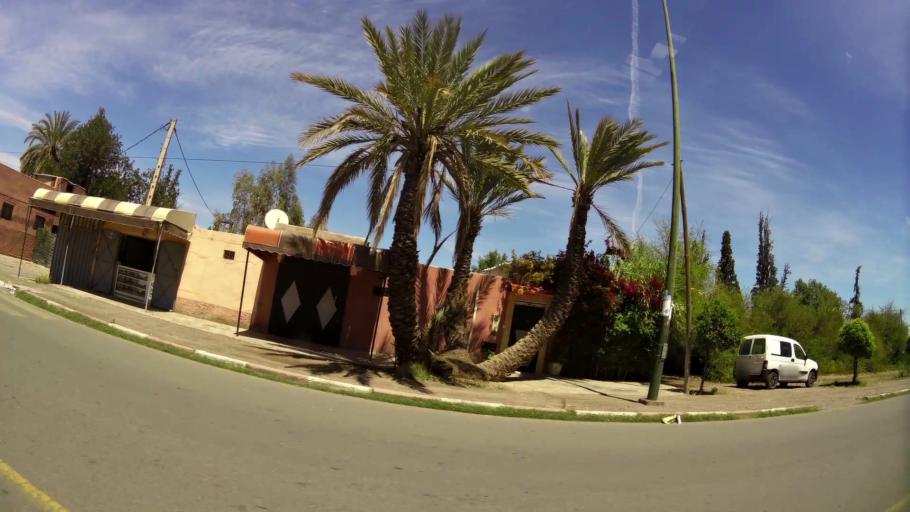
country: MA
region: Marrakech-Tensift-Al Haouz
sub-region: Marrakech
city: Marrakesh
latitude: 31.6355
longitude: -8.0467
